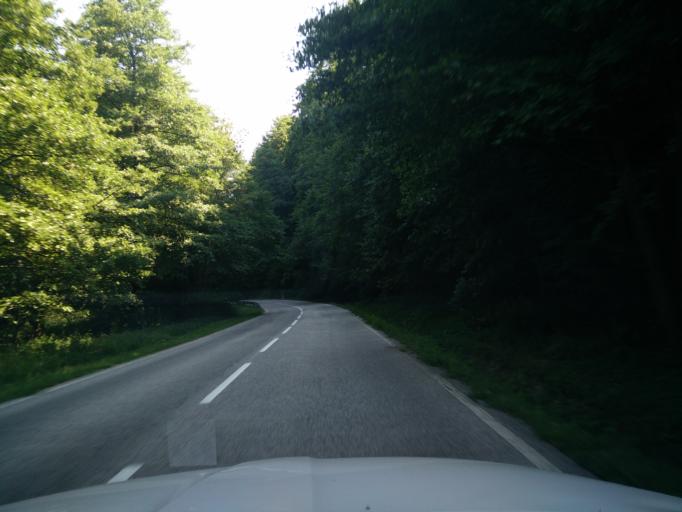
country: SK
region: Nitriansky
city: Bojnice
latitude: 48.8482
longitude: 18.4685
